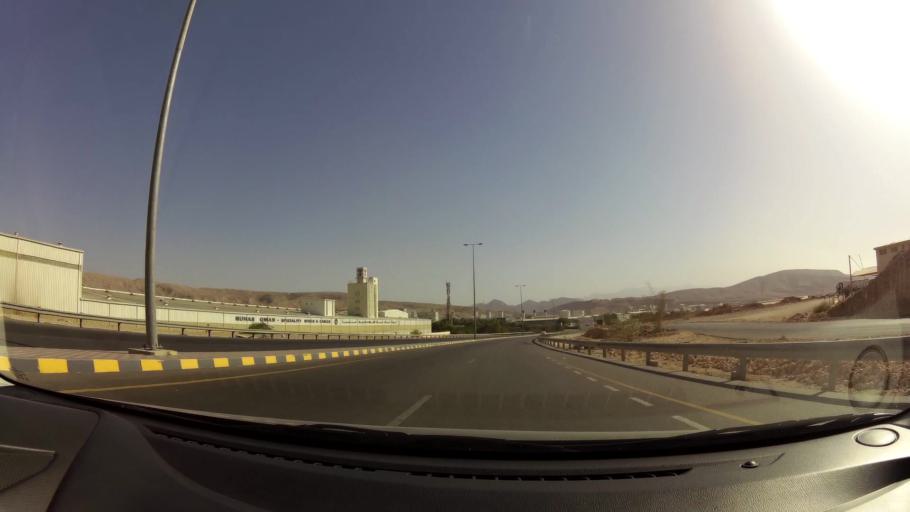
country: OM
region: Muhafazat Masqat
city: As Sib al Jadidah
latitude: 23.5606
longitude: 58.2051
